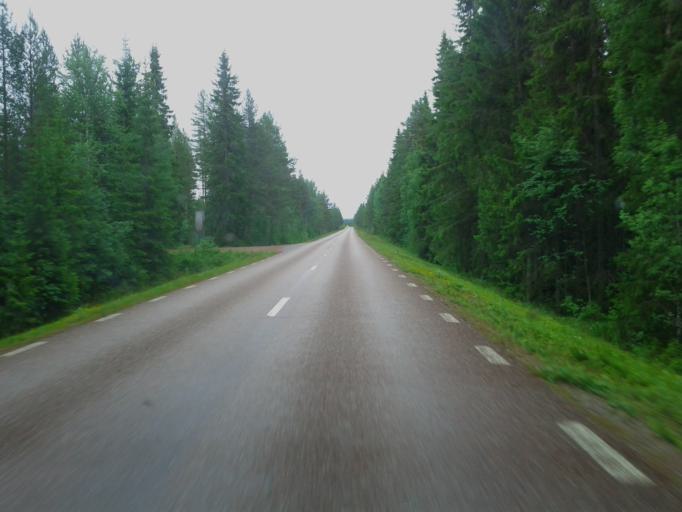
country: NO
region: Hedmark
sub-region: Trysil
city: Innbygda
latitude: 61.8136
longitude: 12.9013
